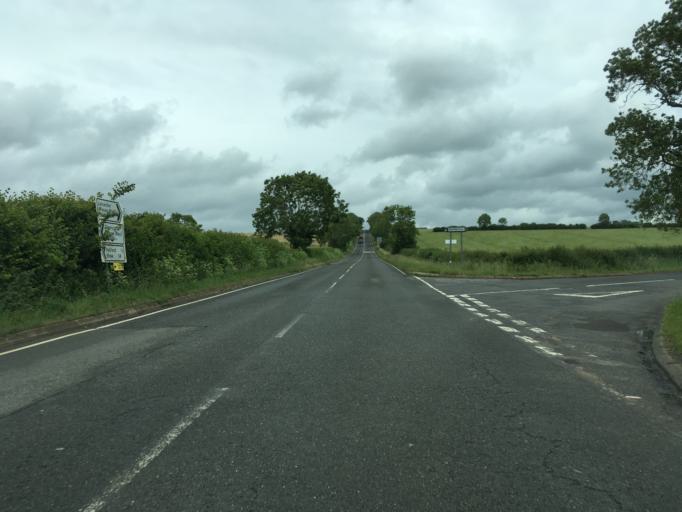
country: GB
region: England
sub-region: Warwickshire
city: Shipston on Stour
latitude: 52.1155
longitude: -1.6138
